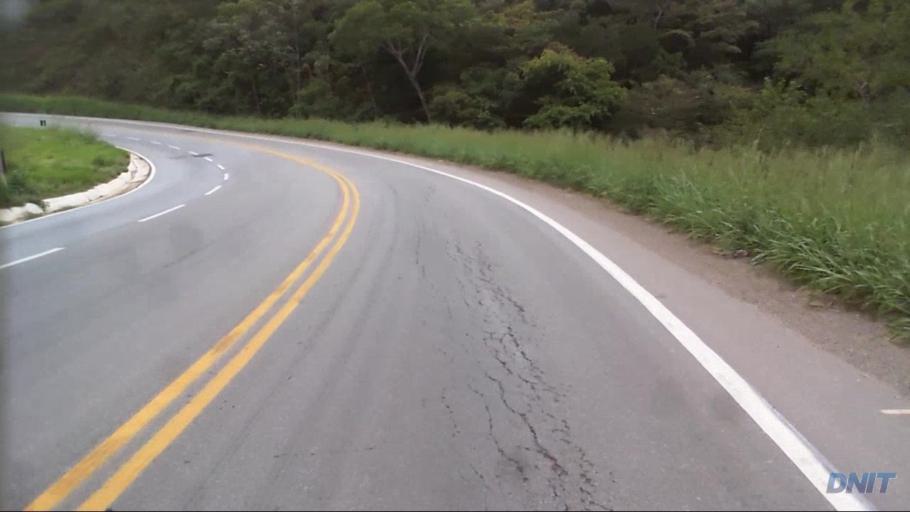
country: BR
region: Minas Gerais
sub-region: Joao Monlevade
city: Joao Monlevade
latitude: -19.8419
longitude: -43.3153
